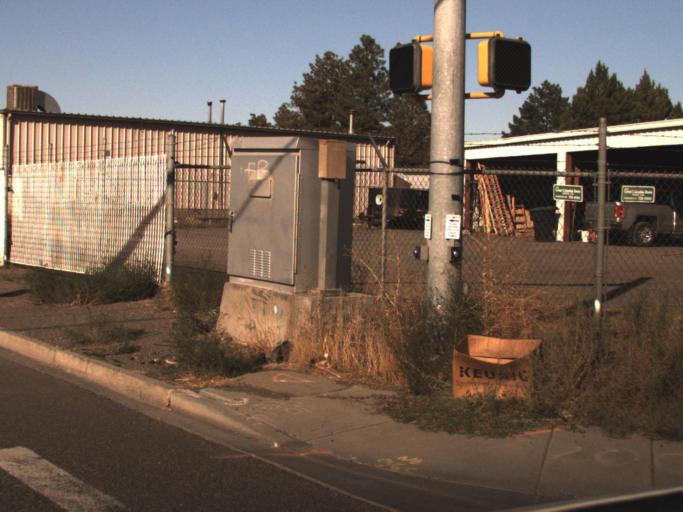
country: US
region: Washington
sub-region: Franklin County
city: Pasco
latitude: 46.2267
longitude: -119.0768
